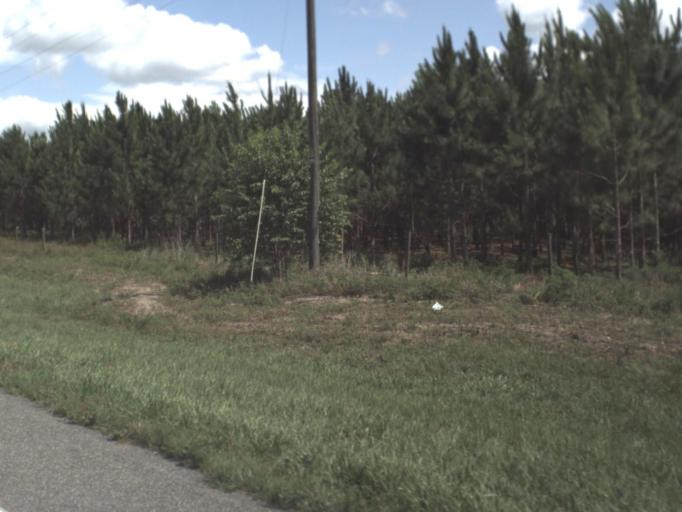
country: US
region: Florida
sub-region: Lafayette County
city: Mayo
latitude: 30.0523
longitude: -83.0899
